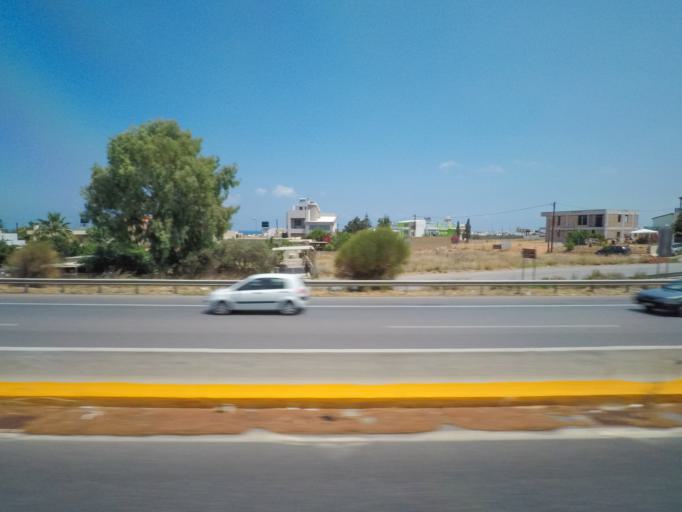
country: GR
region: Crete
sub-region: Nomos Irakleiou
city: Kokkini Hani
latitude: 35.3256
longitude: 25.2570
